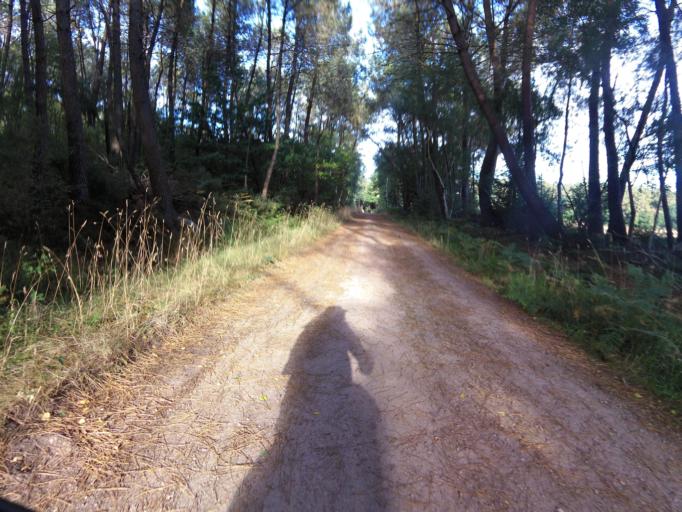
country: FR
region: Brittany
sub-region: Departement du Morbihan
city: Molac
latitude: 47.7376
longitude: -2.4267
